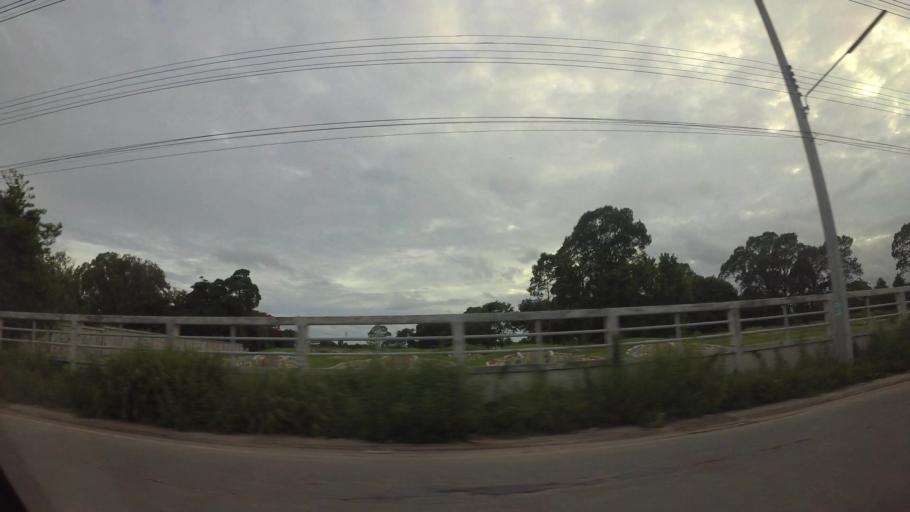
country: TH
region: Rayong
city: Rayong
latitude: 12.6718
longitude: 101.2634
